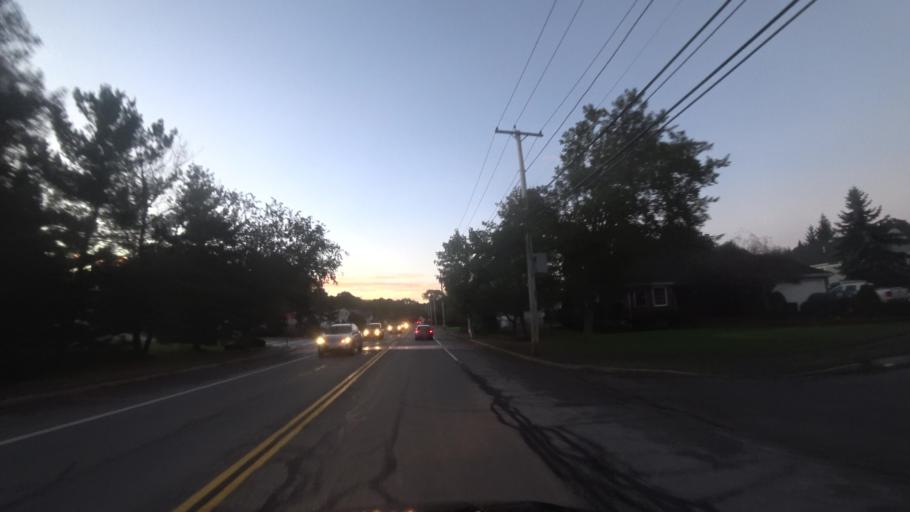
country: US
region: Massachusetts
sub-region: Essex County
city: Saugus
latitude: 42.4770
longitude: -71.0395
